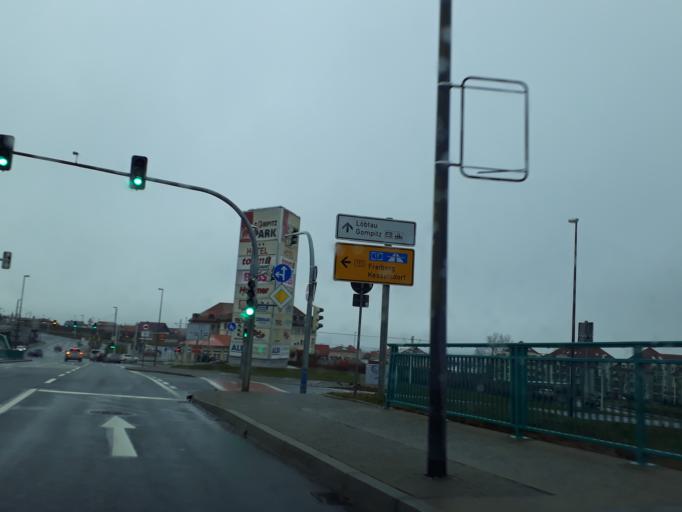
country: DE
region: Saxony
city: Freital
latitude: 51.0381
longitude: 13.6331
